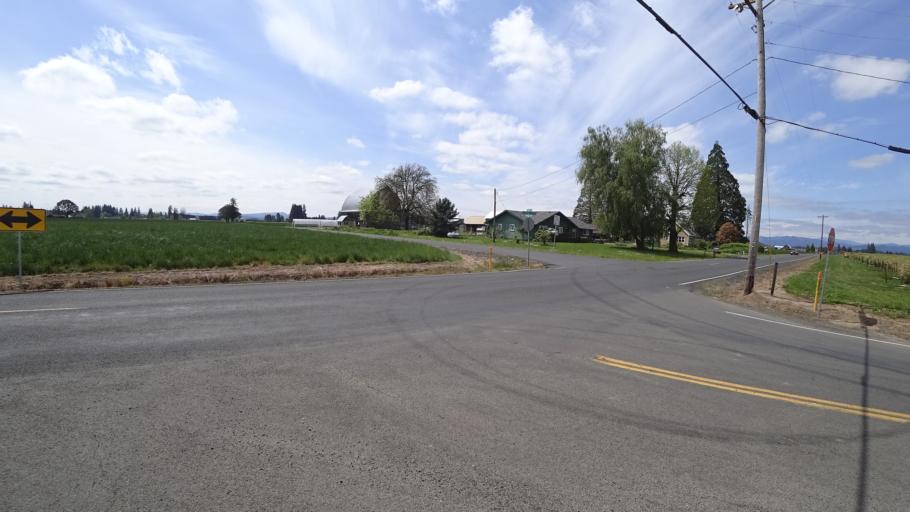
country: US
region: Oregon
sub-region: Washington County
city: Hillsboro
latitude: 45.5440
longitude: -123.0125
